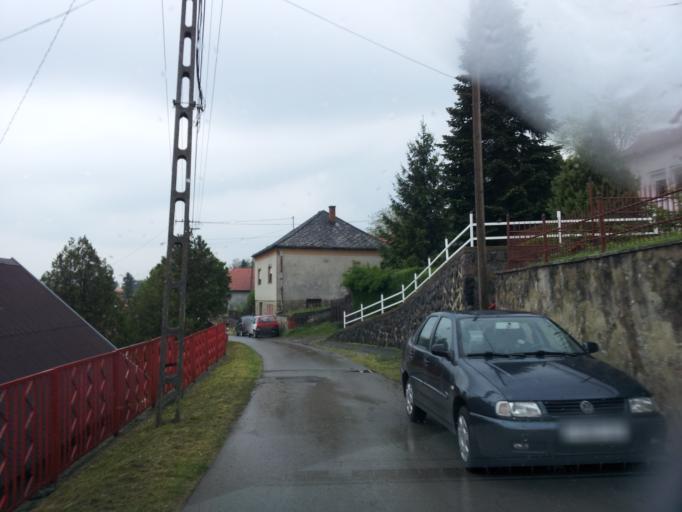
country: HU
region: Baranya
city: Hosszuheteny
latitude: 46.1683
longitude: 18.3476
